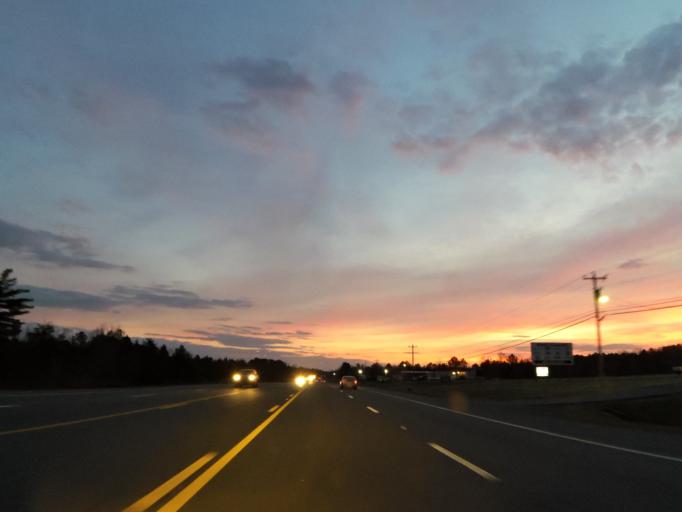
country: US
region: Tennessee
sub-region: Polk County
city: Benton
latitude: 35.1571
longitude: -84.7030
